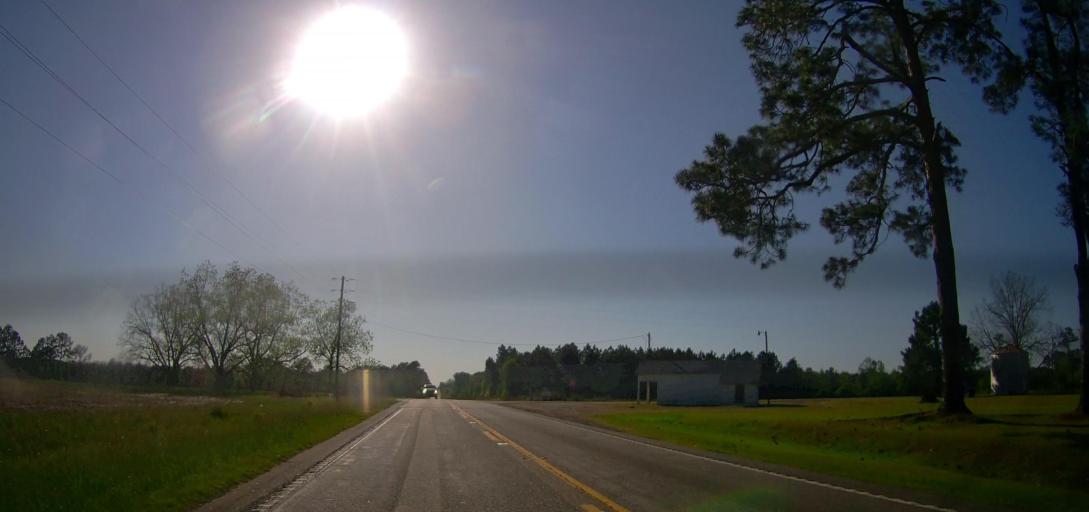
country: US
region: Georgia
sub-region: Ben Hill County
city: Fitzgerald
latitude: 31.7196
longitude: -83.3840
